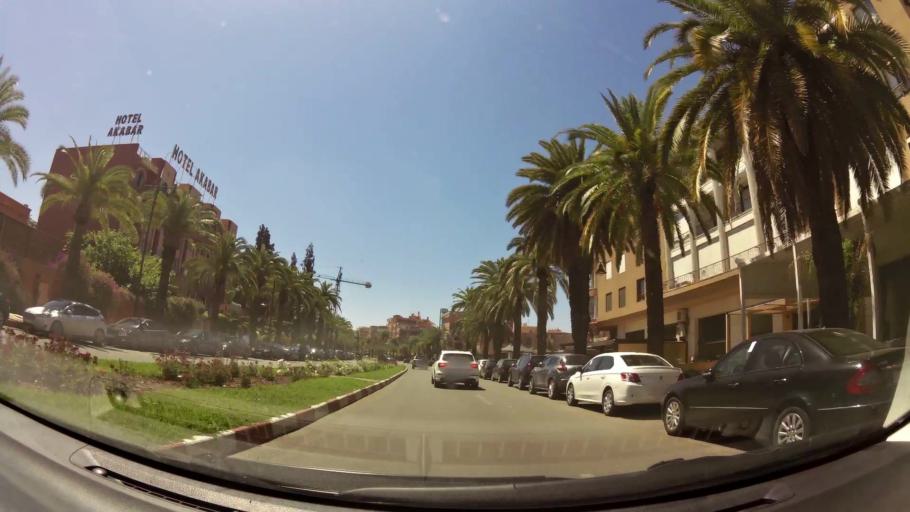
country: MA
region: Marrakech-Tensift-Al Haouz
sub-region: Marrakech
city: Marrakesh
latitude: 31.6267
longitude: -8.0041
